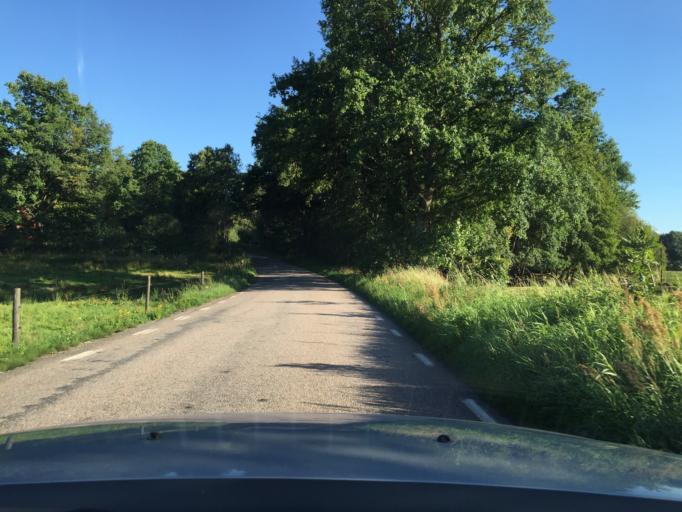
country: SE
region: Skane
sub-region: Hassleholms Kommun
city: Sosdala
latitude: 56.0466
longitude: 13.7223
